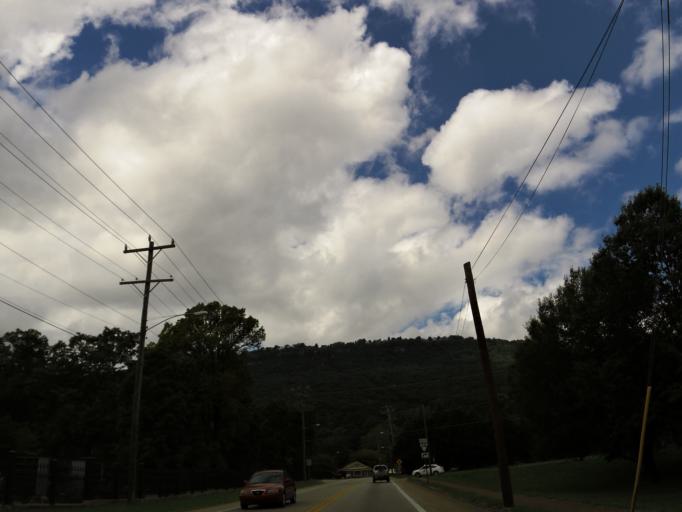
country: US
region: Tennessee
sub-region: Hamilton County
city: Lookout Mountain
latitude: 35.0081
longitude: -85.3254
